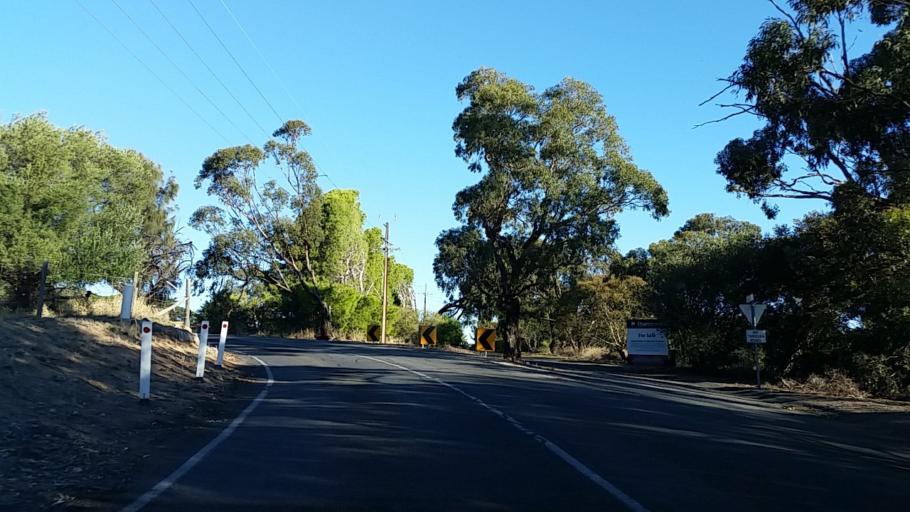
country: AU
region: South Australia
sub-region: Onkaparinga
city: Hackham
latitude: -35.1515
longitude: 138.5383
